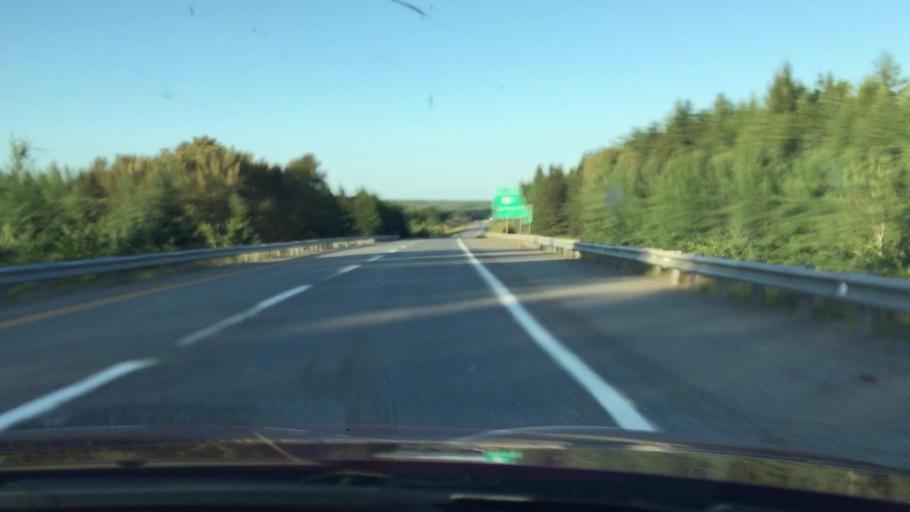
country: US
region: Maine
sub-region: Aroostook County
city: Hodgdon
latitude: 46.1357
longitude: -68.0817
